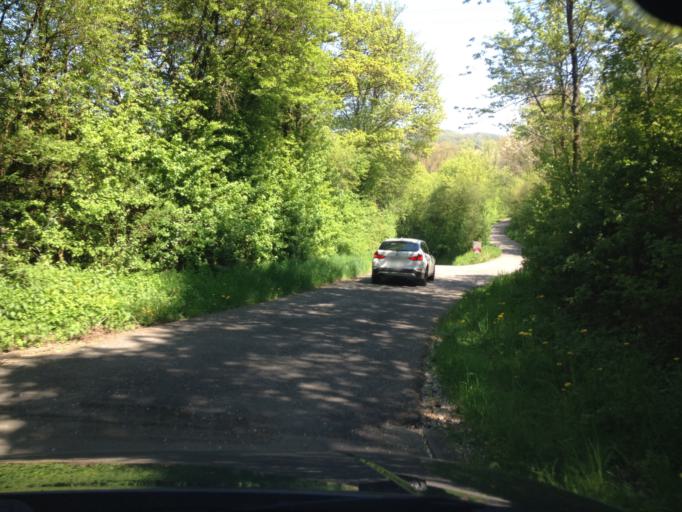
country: DE
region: Saarland
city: Ottweiler
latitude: 49.3817
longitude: 7.1773
